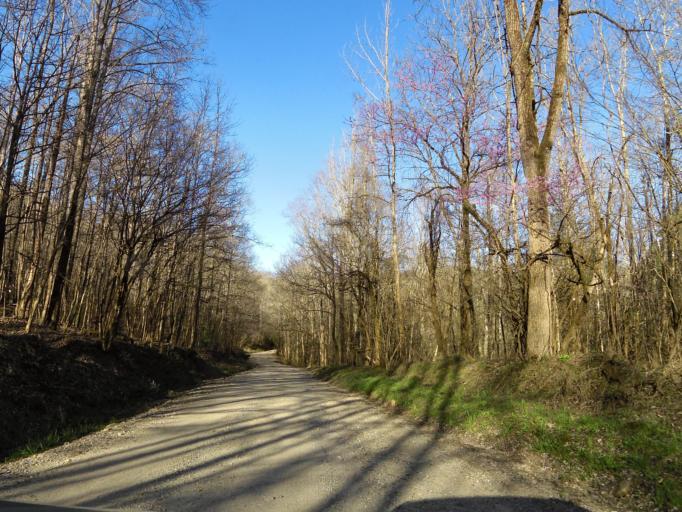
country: US
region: Tennessee
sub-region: Scott County
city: Huntsville
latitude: 36.2454
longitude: -84.4070
